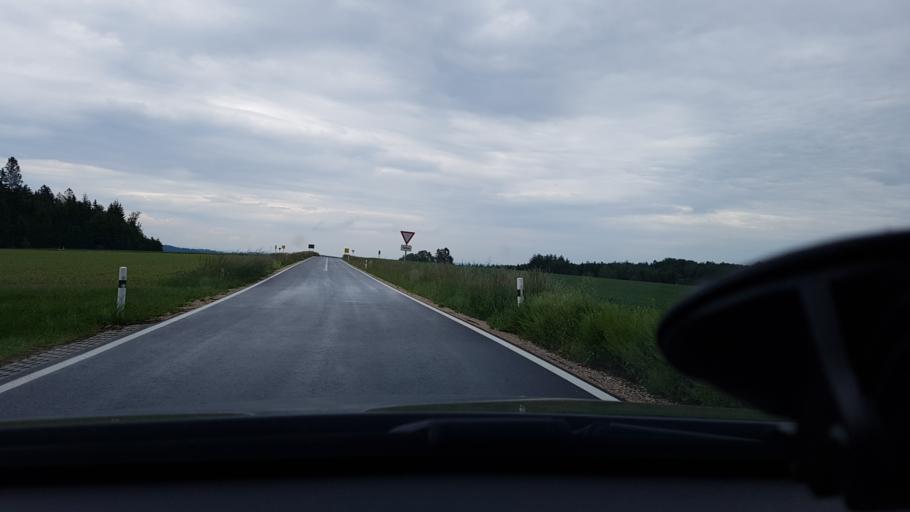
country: DE
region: Bavaria
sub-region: Lower Bavaria
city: Stubenberg
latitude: 48.3305
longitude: 13.0658
